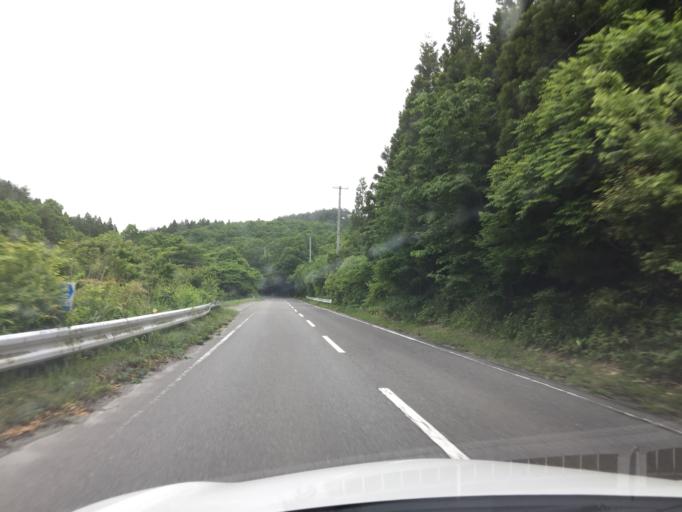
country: JP
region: Fukushima
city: Funehikimachi-funehiki
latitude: 37.3132
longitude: 140.7081
